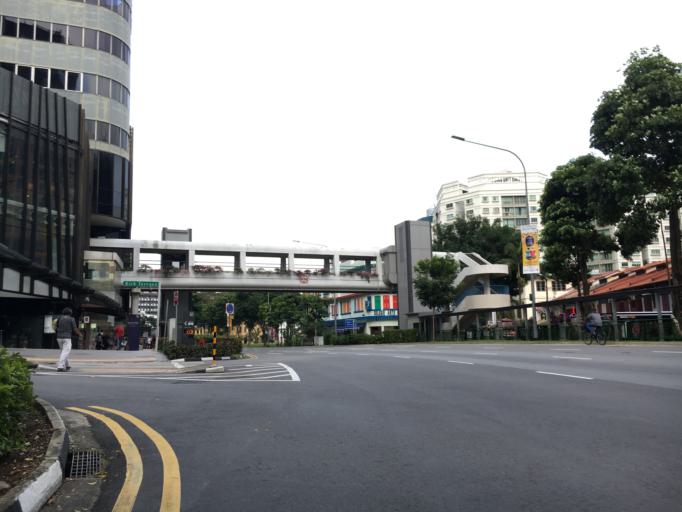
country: SG
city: Singapore
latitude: 1.2996
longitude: 103.8494
